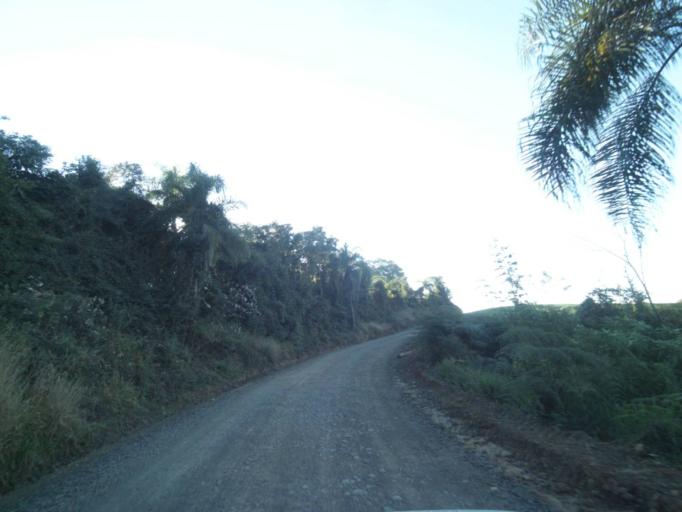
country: BR
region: Parana
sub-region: Telemaco Borba
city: Telemaco Borba
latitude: -24.4615
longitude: -50.5987
